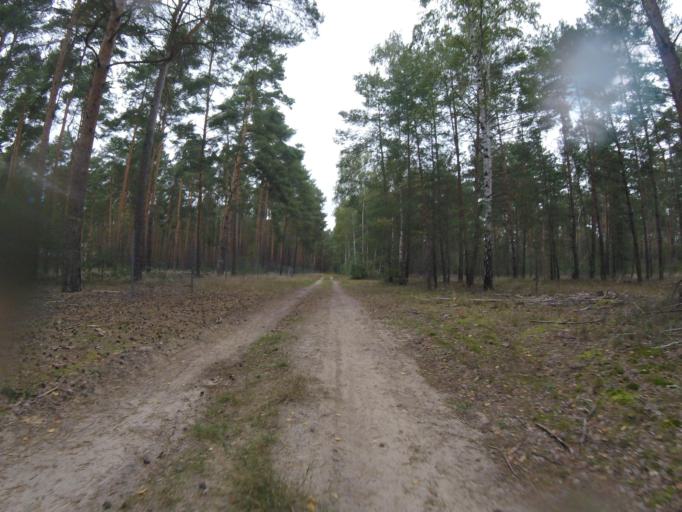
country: DE
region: Brandenburg
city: Gross Koris
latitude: 52.1825
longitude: 13.6772
